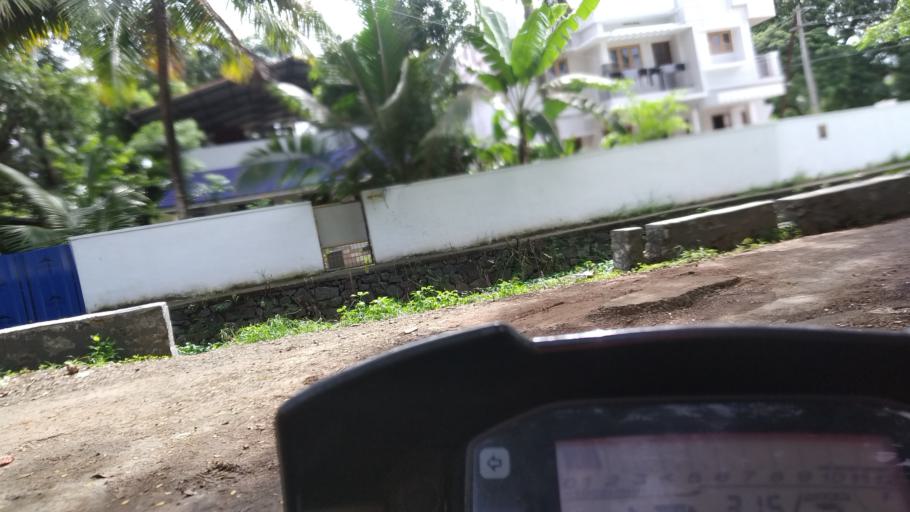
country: IN
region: Kerala
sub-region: Ernakulam
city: Cochin
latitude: 9.9806
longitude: 76.2917
